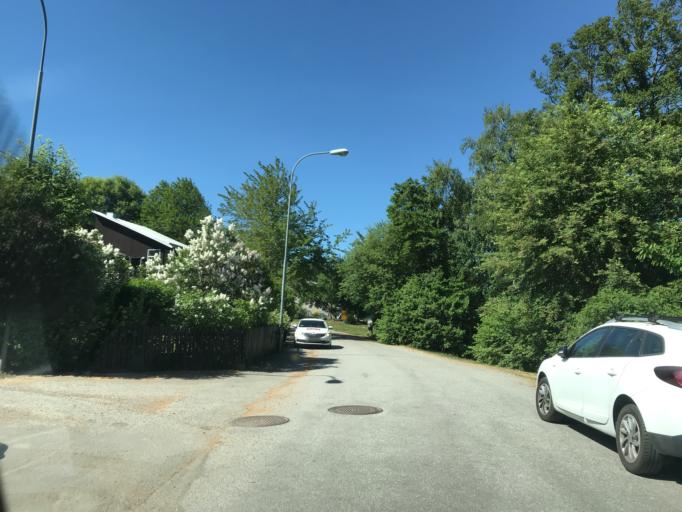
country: SE
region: Stockholm
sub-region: Sollentuna Kommun
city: Sollentuna
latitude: 59.4239
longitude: 17.9754
